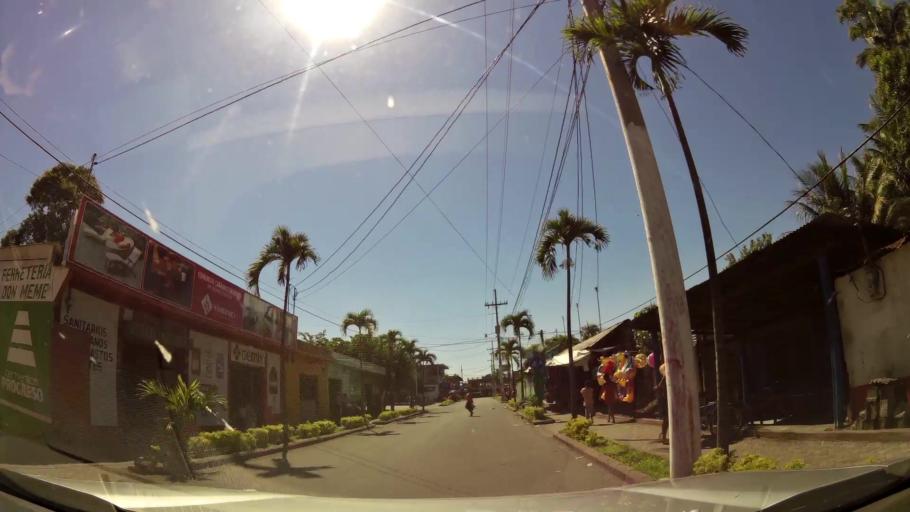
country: GT
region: Escuintla
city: Iztapa
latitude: 13.9321
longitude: -90.7148
